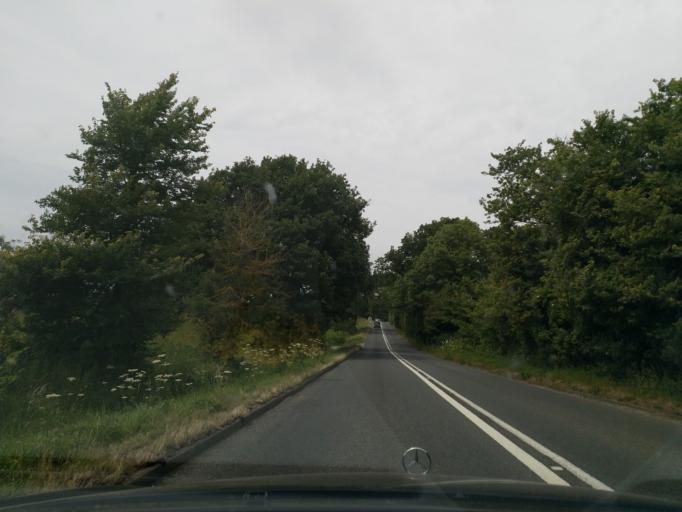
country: GB
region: England
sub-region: Solihull
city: Balsall Common
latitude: 52.3781
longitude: -1.6381
